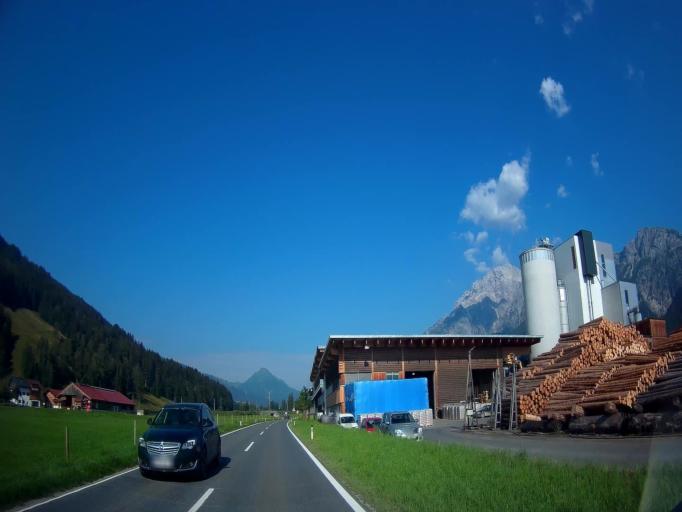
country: AT
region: Salzburg
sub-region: Politischer Bezirk Zell am See
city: Saalfelden am Steinernen Meer
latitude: 47.4402
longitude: 12.8121
